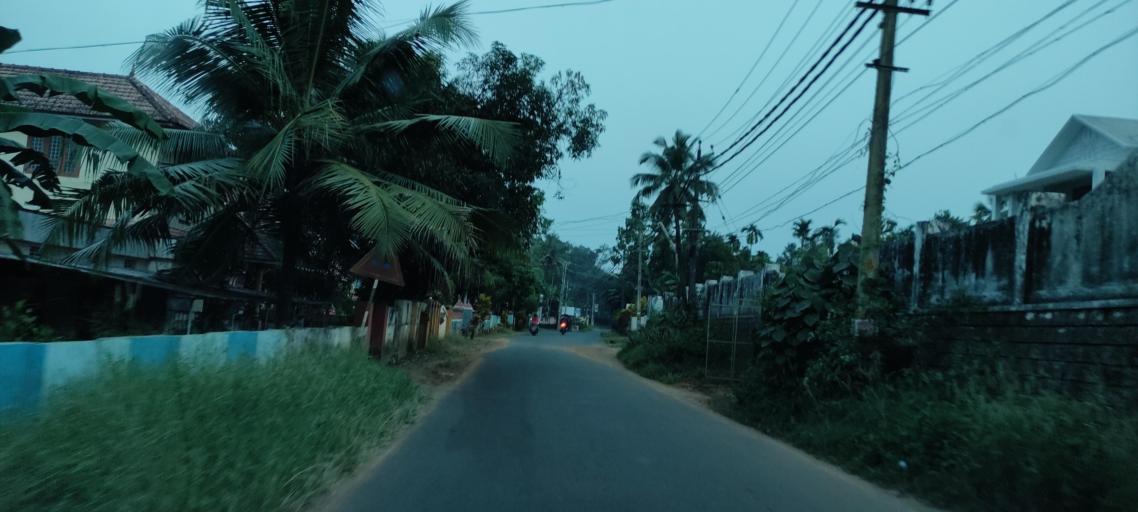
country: IN
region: Kerala
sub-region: Pattanamtitta
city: Adur
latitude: 9.1596
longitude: 76.7493
